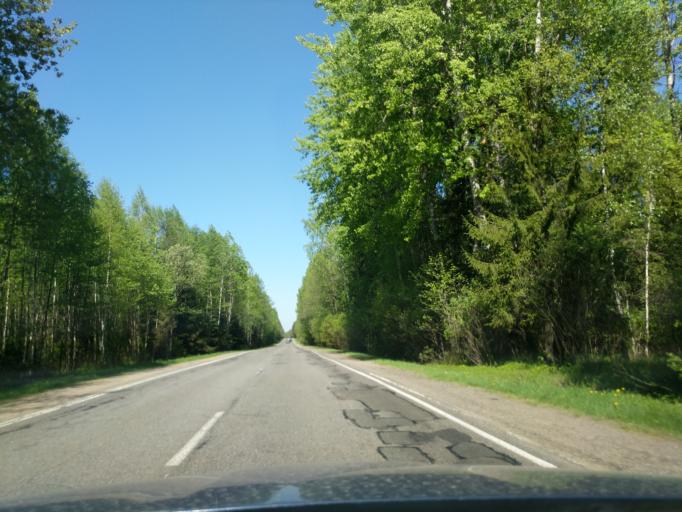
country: BY
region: Minsk
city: Il'ya
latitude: 54.4026
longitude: 27.3238
